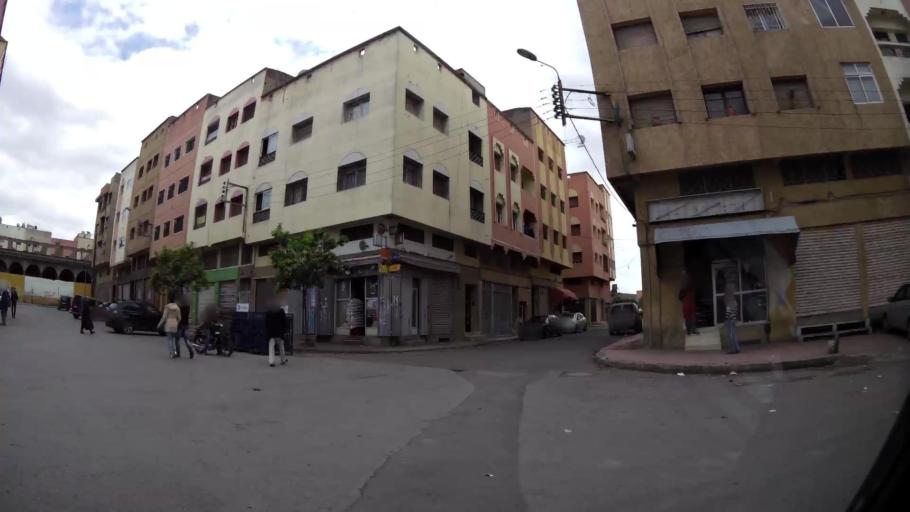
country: MA
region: Grand Casablanca
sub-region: Casablanca
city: Casablanca
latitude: 33.5744
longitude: -7.5684
